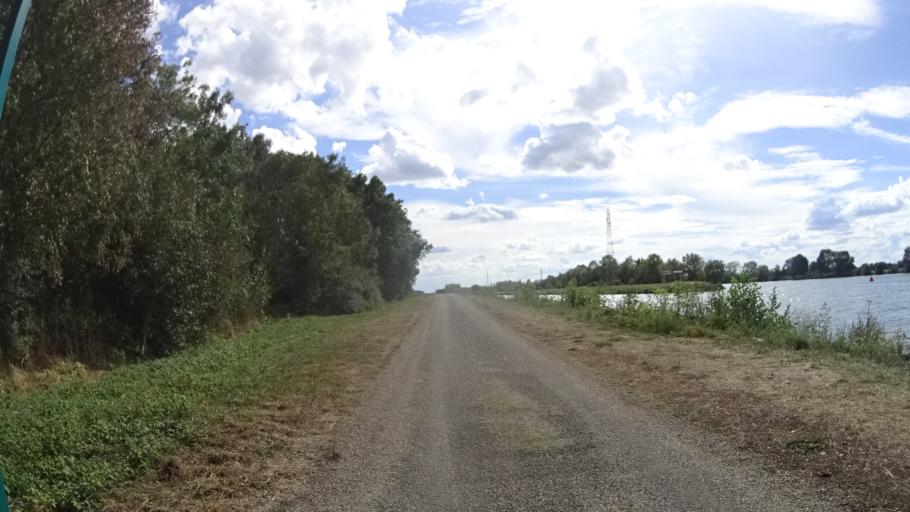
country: FR
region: Bourgogne
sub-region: Departement de la Cote-d'Or
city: Losne
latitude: 47.0724
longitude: 5.2047
